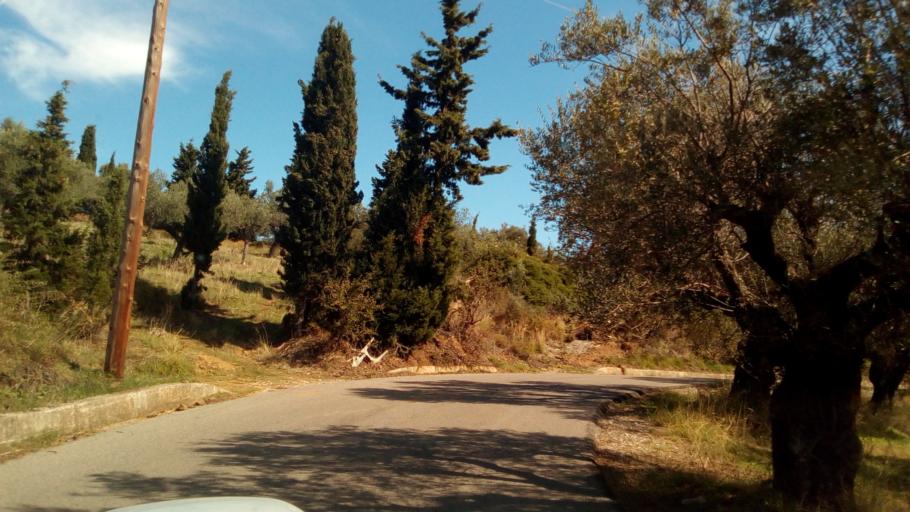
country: GR
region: West Greece
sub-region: Nomos Aitolias kai Akarnanias
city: Antirrio
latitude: 38.3611
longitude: 21.7561
